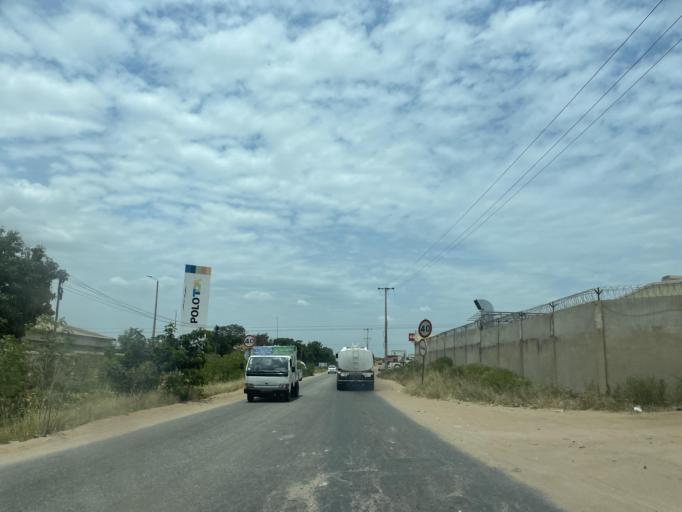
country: AO
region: Luanda
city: Luanda
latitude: -8.9293
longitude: 13.3950
